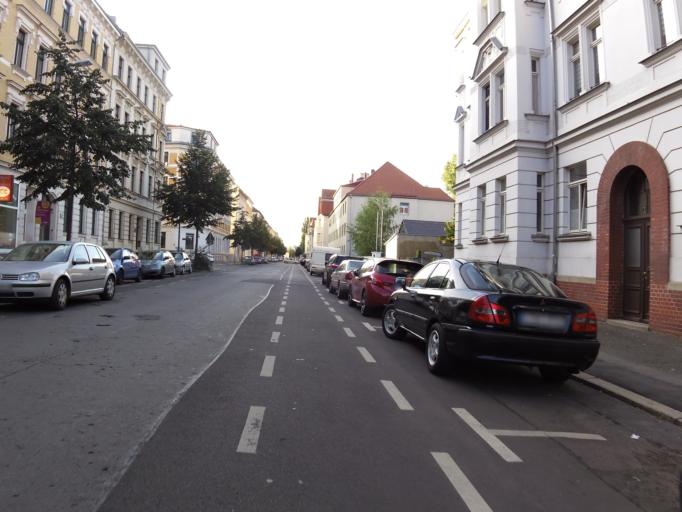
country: DE
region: Saxony
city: Leipzig
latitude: 51.3422
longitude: 12.3264
